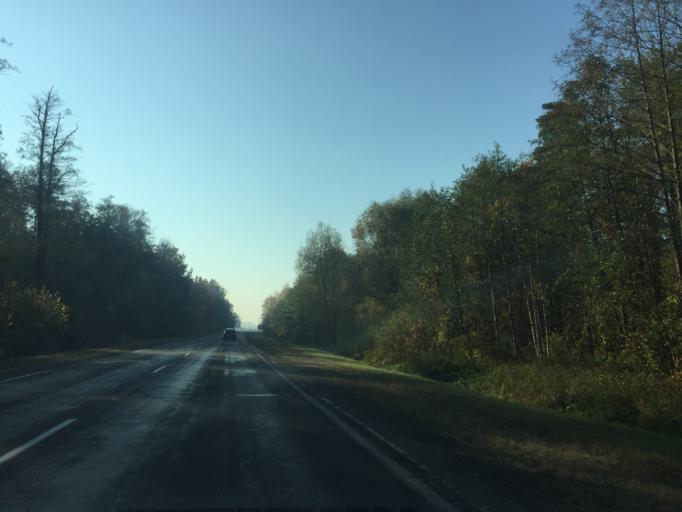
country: BY
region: Gomel
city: Gomel
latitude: 52.4020
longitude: 30.8291
